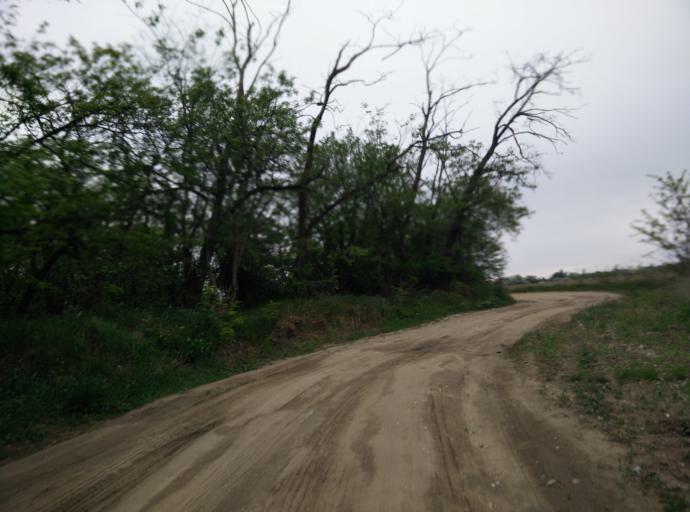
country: HU
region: Pest
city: Dunakeszi
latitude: 47.6064
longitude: 19.1491
